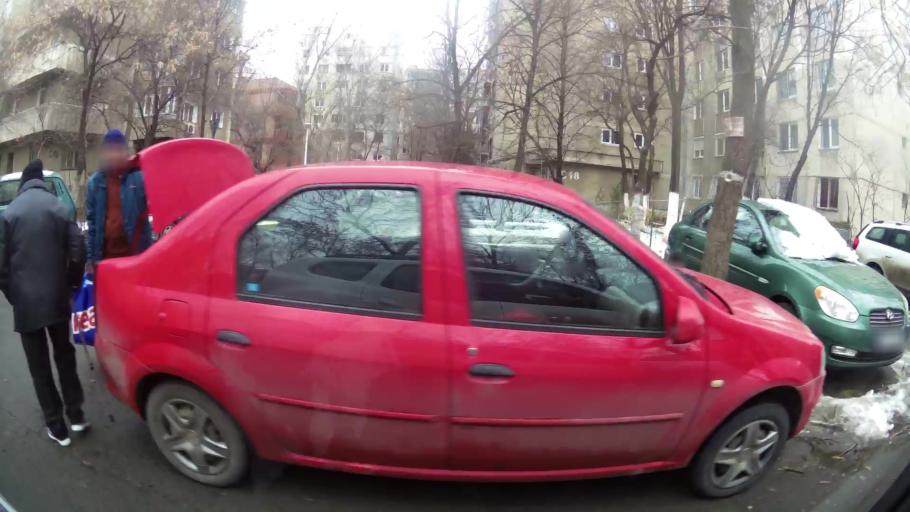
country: RO
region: Ilfov
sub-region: Comuna Chiajna
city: Rosu
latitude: 44.4174
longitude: 26.0453
